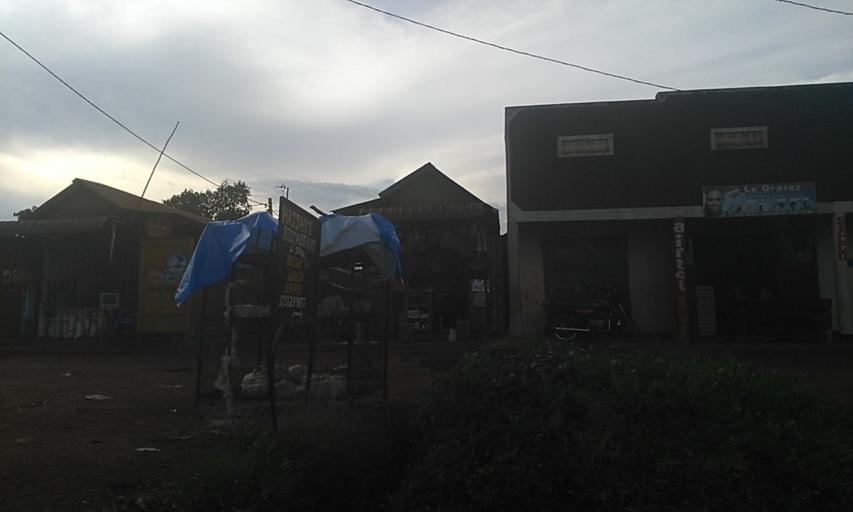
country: UG
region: Central Region
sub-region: Wakiso District
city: Kajansi
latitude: 0.2542
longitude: 32.5062
